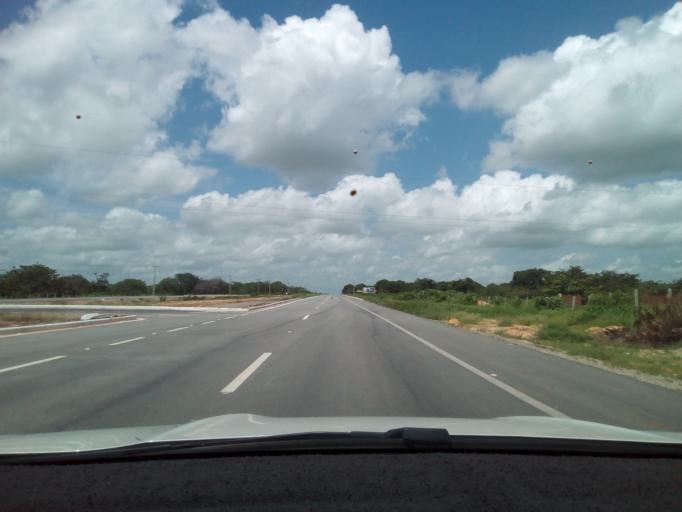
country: BR
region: Ceara
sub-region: Aracati
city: Aracati
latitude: -4.5349
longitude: -37.7993
